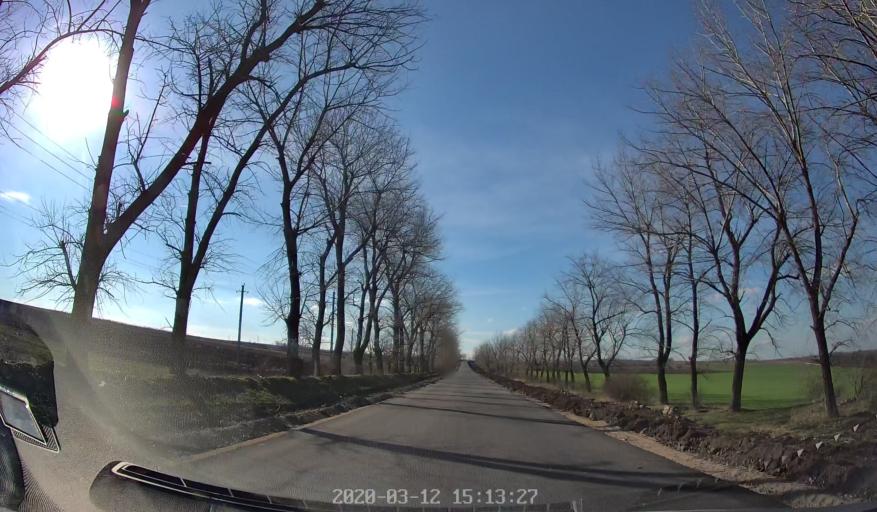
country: MD
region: Chisinau
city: Ciorescu
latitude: 47.2301
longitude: 28.9644
